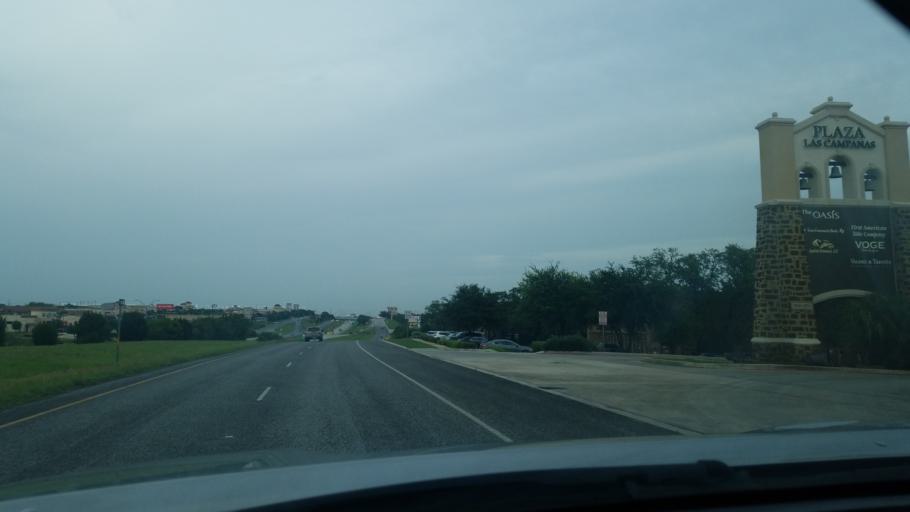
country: US
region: Texas
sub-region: Bexar County
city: Hollywood Park
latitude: 29.6081
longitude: -98.5217
